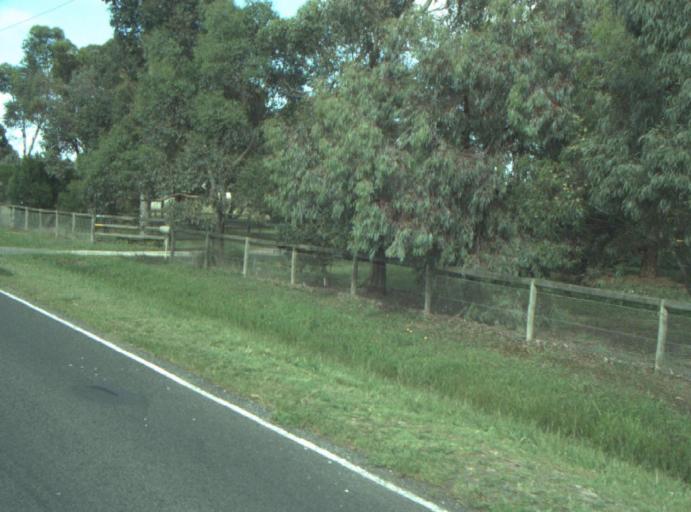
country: AU
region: Victoria
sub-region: Greater Geelong
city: Lara
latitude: -38.0134
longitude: 144.4242
